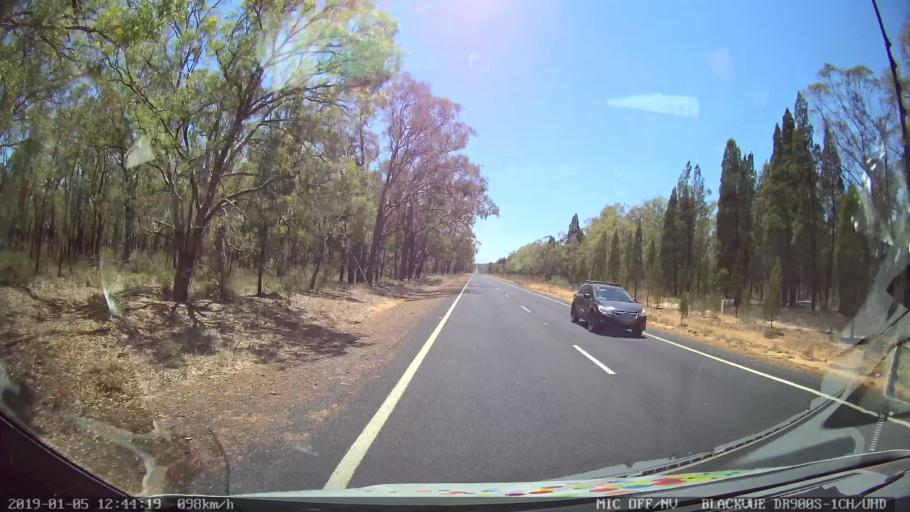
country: AU
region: New South Wales
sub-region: Warrumbungle Shire
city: Coonabarabran
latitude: -31.1390
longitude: 149.5357
